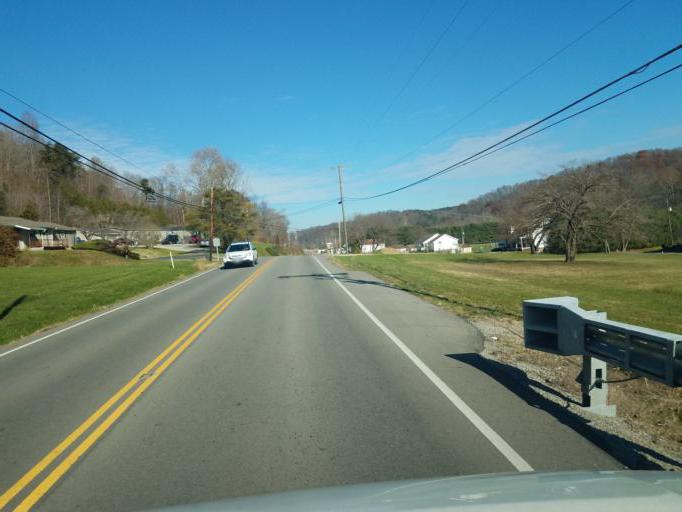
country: US
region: Ohio
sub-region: Scioto County
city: Rosemount
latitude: 38.8324
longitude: -82.9212
